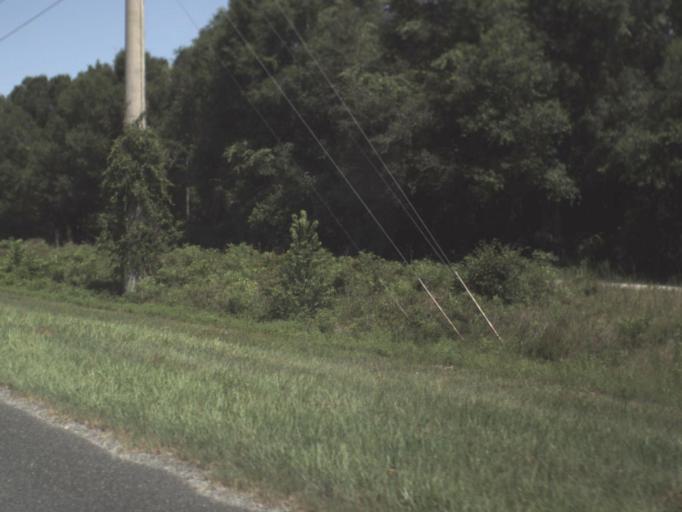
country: US
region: Florida
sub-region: Dixie County
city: Cross City
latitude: 29.6037
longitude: -83.0261
